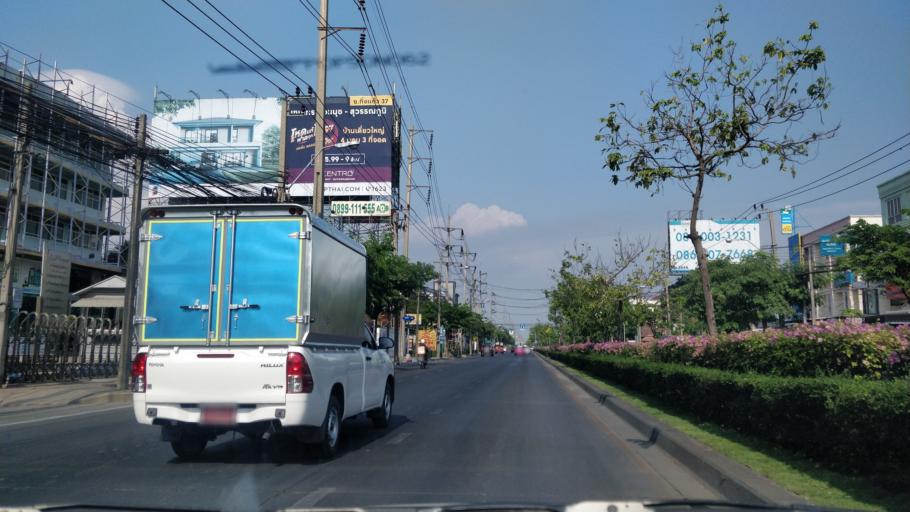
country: TH
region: Bangkok
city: Suan Luang
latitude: 13.7204
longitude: 100.6801
